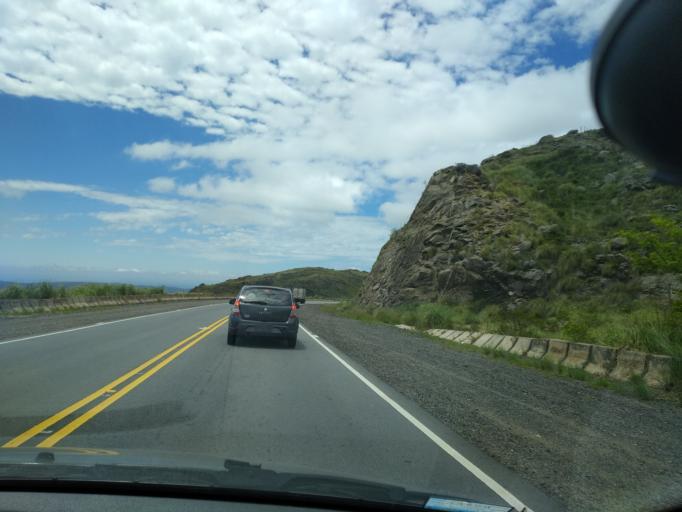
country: AR
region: Cordoba
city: Cuesta Blanca
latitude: -31.5977
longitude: -64.7044
